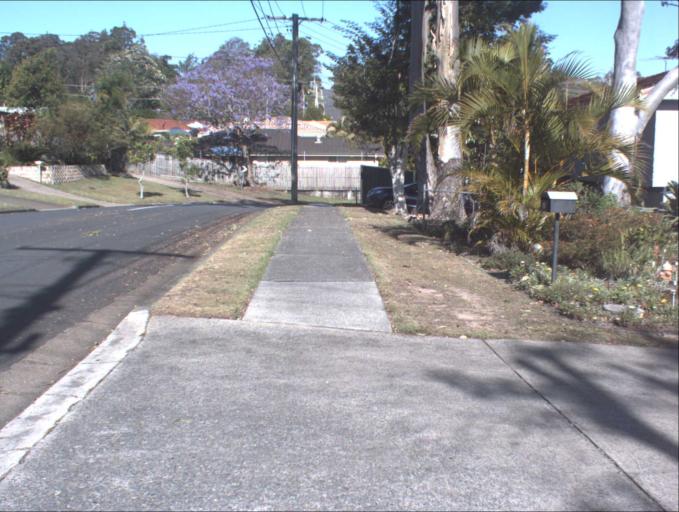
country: AU
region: Queensland
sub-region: Logan
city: Rochedale South
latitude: -27.6016
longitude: 153.1195
